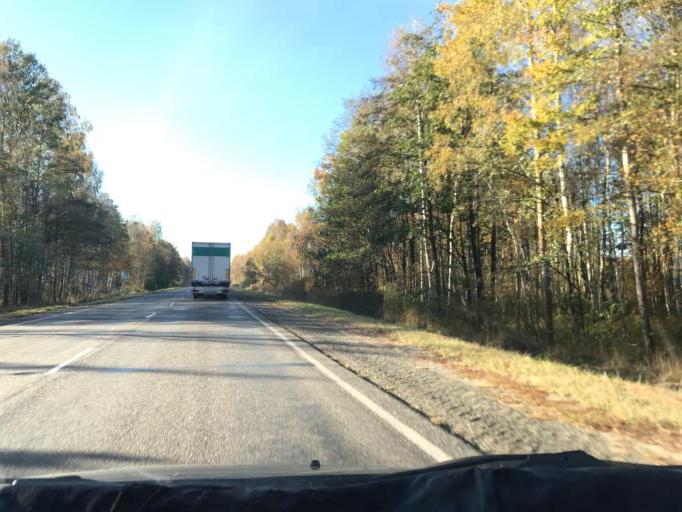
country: BY
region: Gomel
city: Mazyr
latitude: 52.1949
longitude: 29.1085
